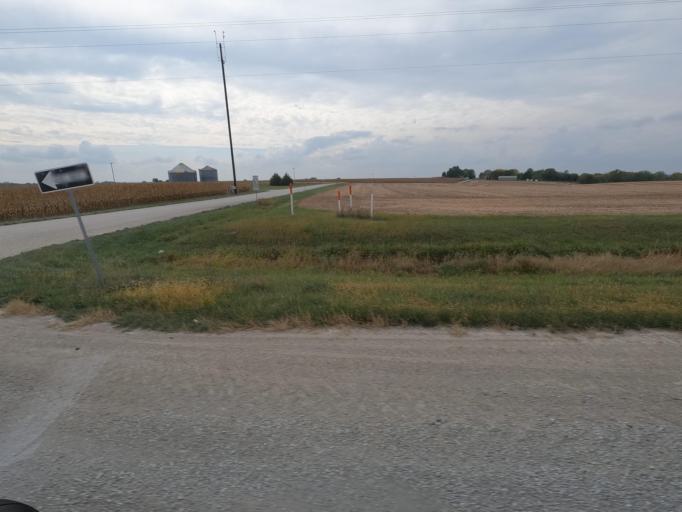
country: US
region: Iowa
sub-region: Jasper County
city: Monroe
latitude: 41.4520
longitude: -93.0257
